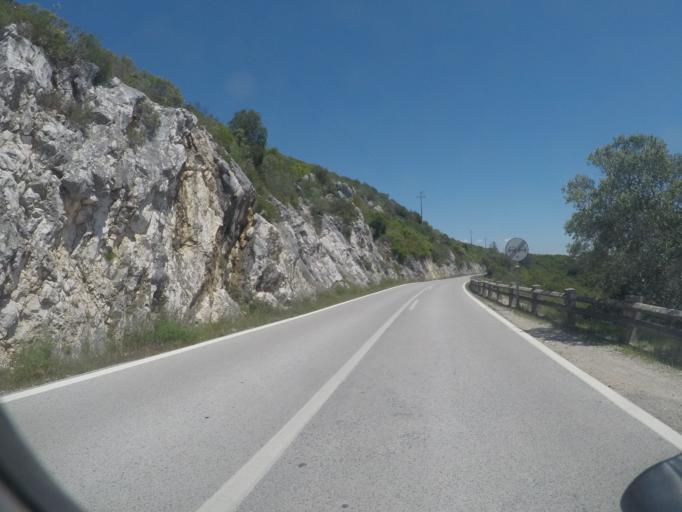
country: PT
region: Setubal
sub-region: Sesimbra
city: Sesimbra
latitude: 38.4603
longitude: -9.0143
